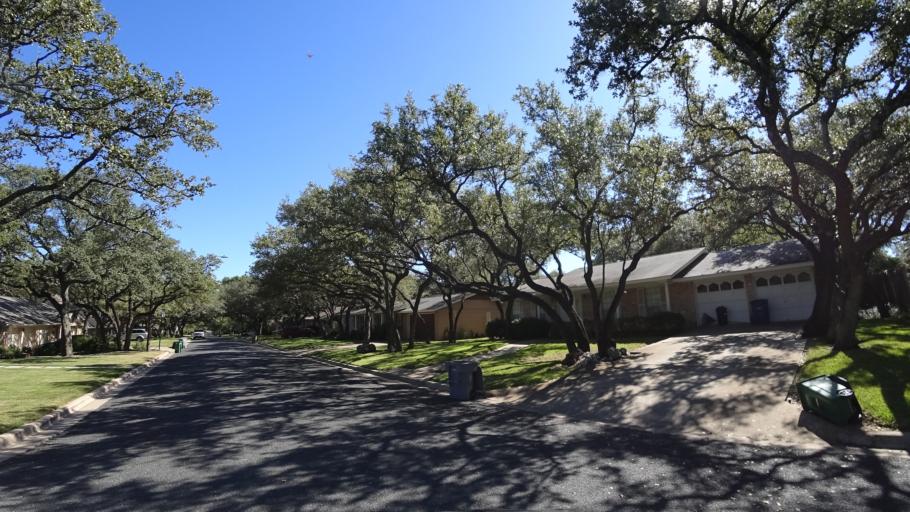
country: US
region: Texas
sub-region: Travis County
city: West Lake Hills
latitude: 30.3631
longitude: -97.7596
